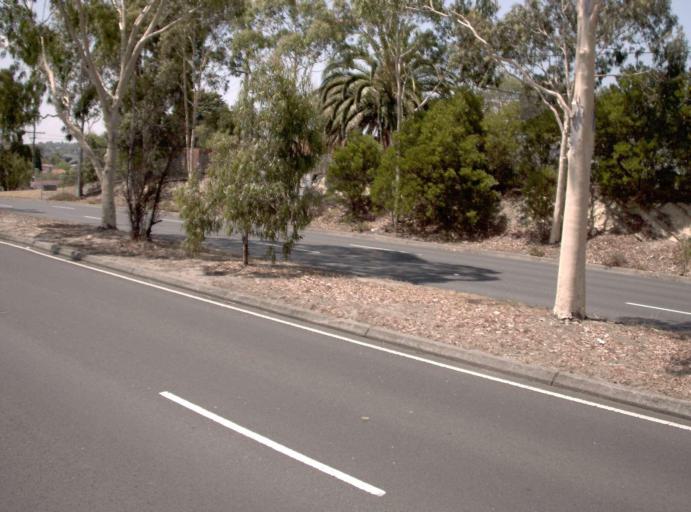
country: AU
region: Victoria
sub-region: Whitehorse
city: Vermont South
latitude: -37.8674
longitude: 145.1681
